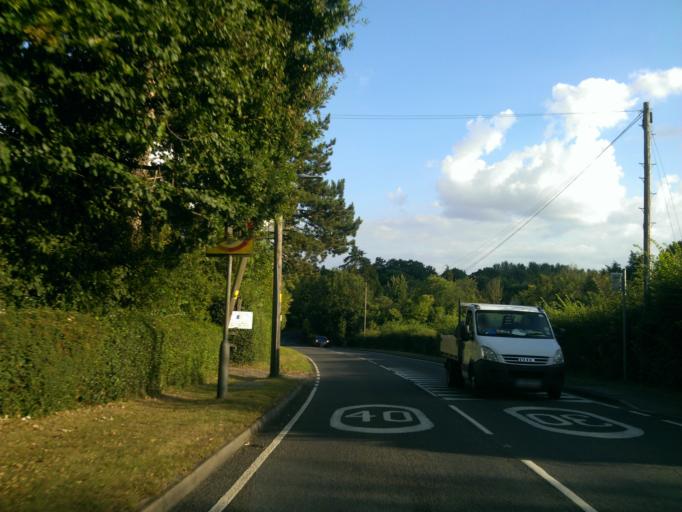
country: GB
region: England
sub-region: Essex
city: Sible Hedingham
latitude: 51.9328
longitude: 0.5948
